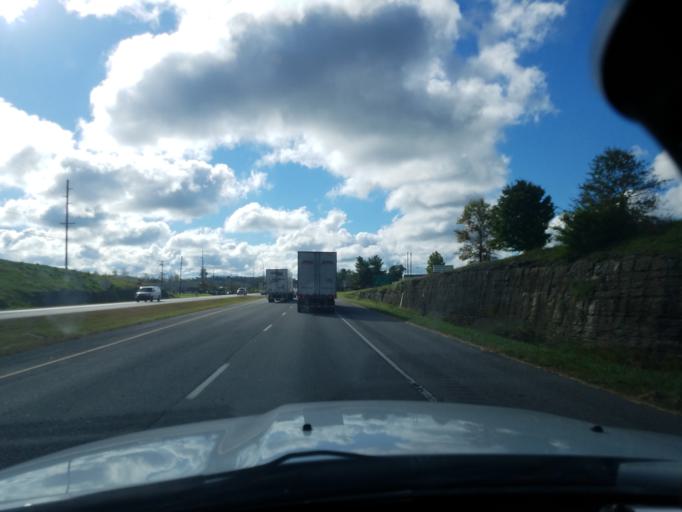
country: US
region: Kentucky
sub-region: Boyle County
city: Danville
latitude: 37.6253
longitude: -84.7962
